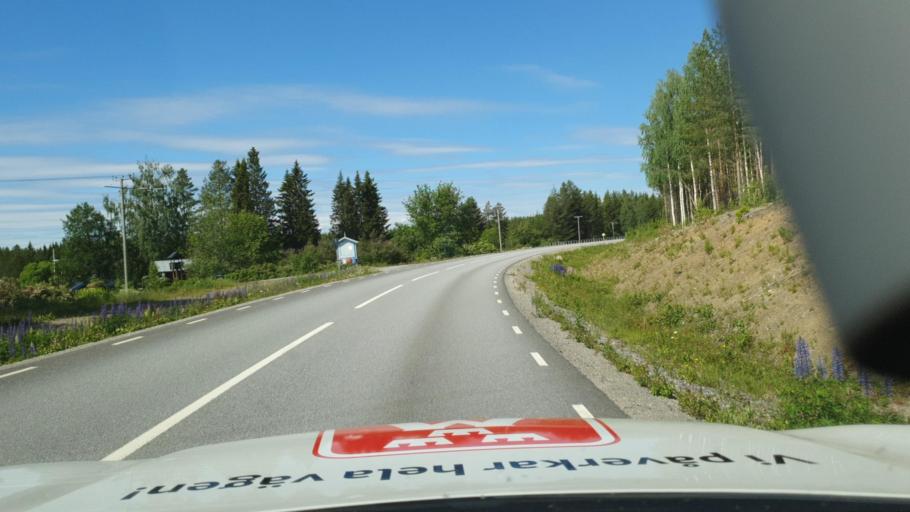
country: SE
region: Vaesterbotten
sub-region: Skelleftea Kommun
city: Boliden
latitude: 64.7403
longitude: 20.3649
